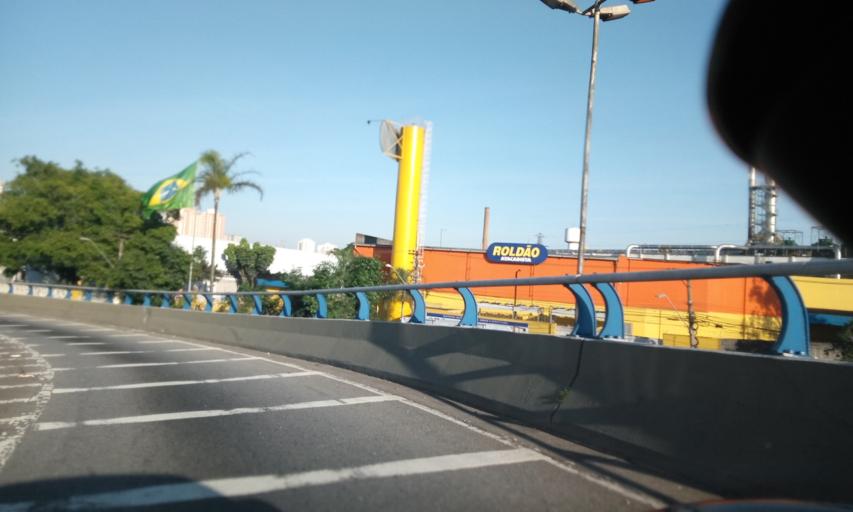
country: BR
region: Sao Paulo
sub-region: Santo Andre
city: Santo Andre
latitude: -23.6632
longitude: -46.5119
